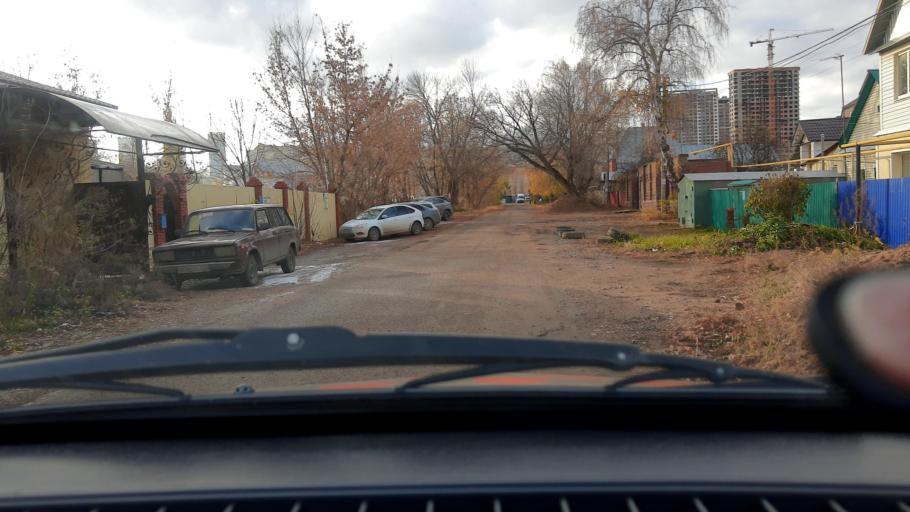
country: RU
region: Bashkortostan
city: Ufa
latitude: 54.7791
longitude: 56.0582
